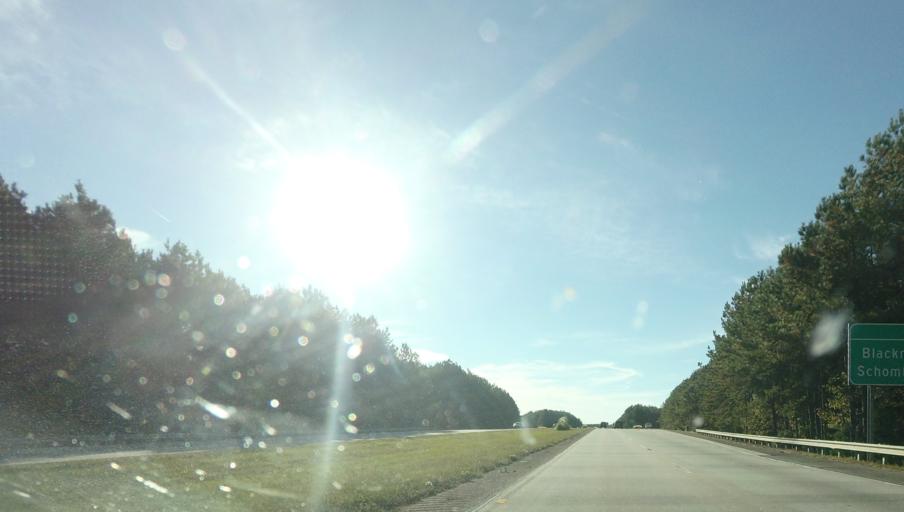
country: US
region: Georgia
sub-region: Muscogee County
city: Columbus
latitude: 32.5553
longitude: -84.8909
